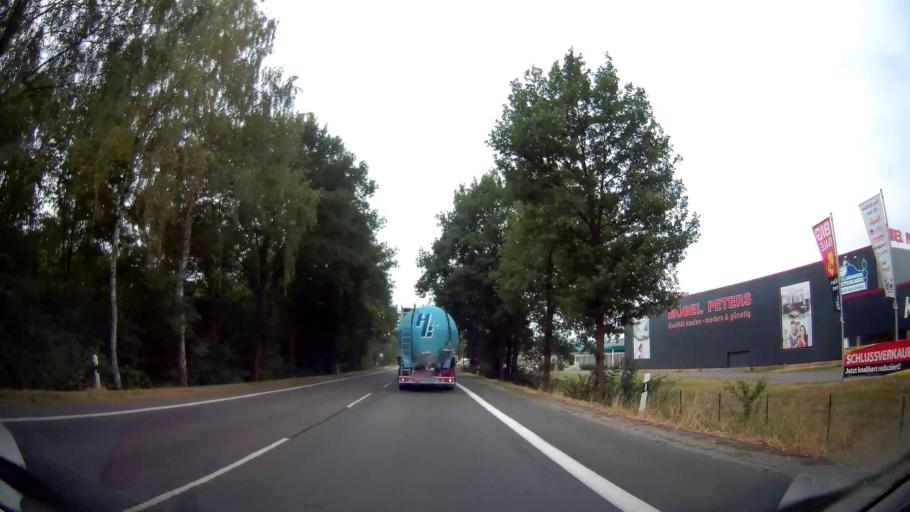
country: DE
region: North Rhine-Westphalia
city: Dorsten
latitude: 51.6564
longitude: 7.0166
